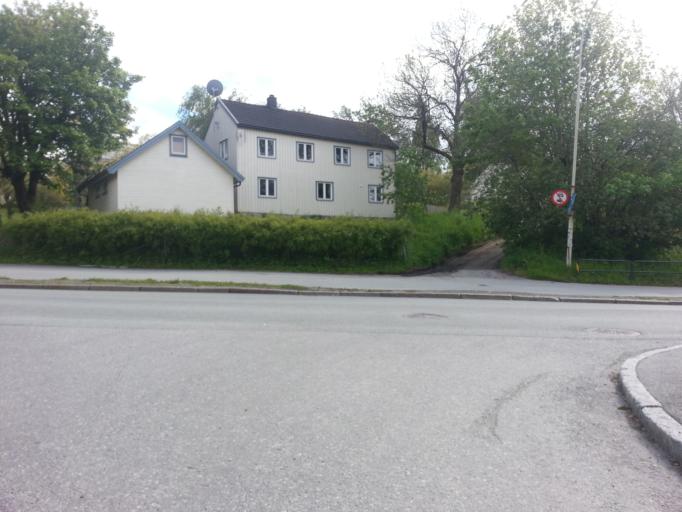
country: NO
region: Sor-Trondelag
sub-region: Trondheim
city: Trondheim
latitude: 63.4214
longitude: 10.4028
